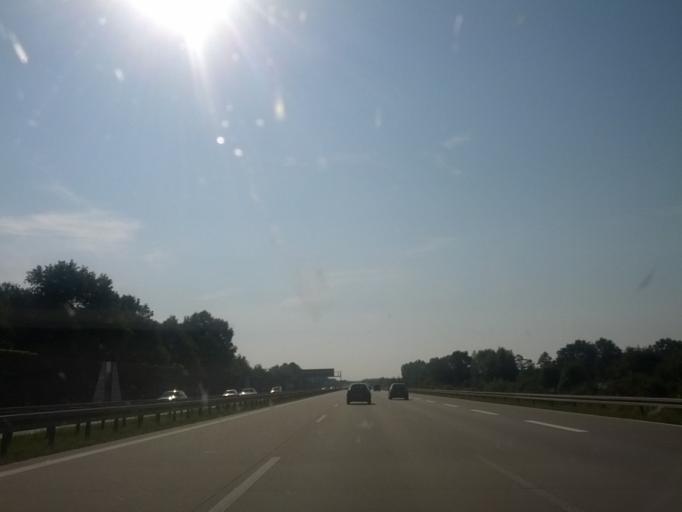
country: DE
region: Brandenburg
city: Ahrensfelde
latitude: 52.5991
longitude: 13.6095
